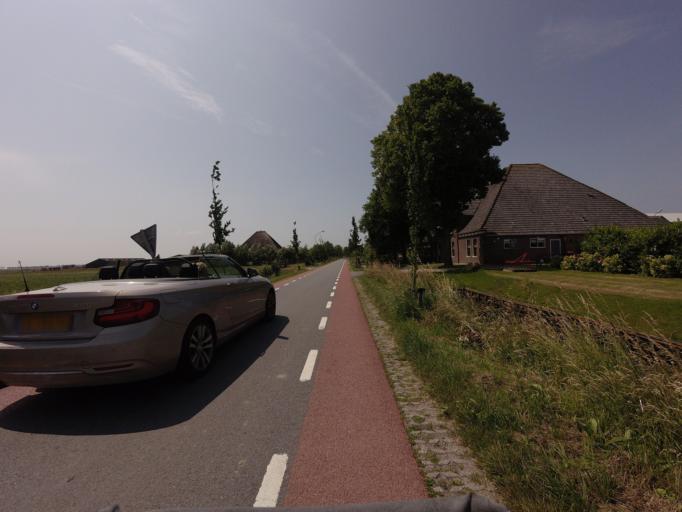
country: NL
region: North Holland
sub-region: Gemeente Opmeer
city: Opmeer
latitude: 52.6569
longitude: 4.9252
